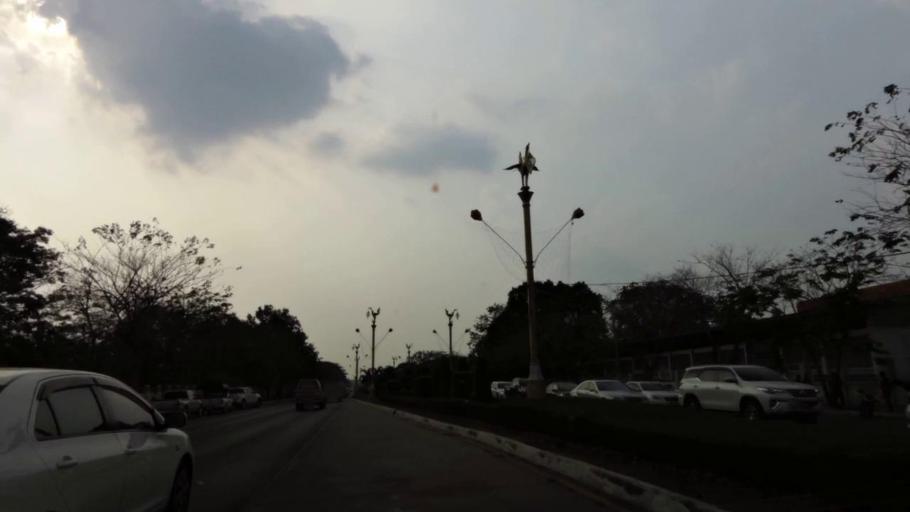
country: TH
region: Phra Nakhon Si Ayutthaya
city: Phra Nakhon Si Ayutthaya
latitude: 14.3504
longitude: 100.5688
